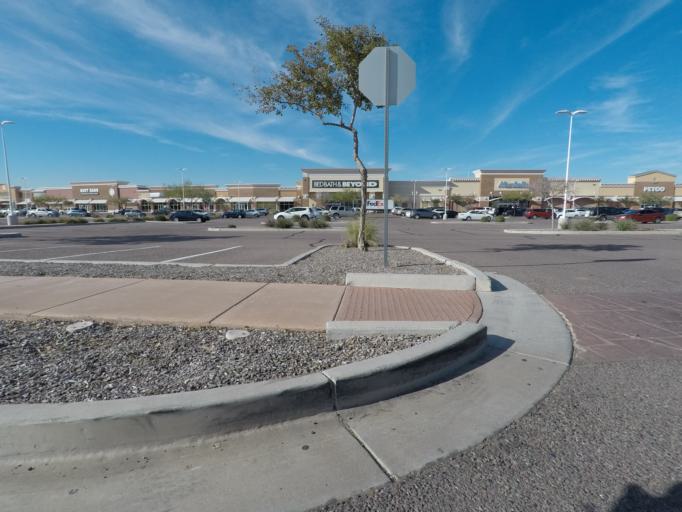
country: US
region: Arizona
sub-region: Maricopa County
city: Tempe
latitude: 33.4315
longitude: -111.8689
